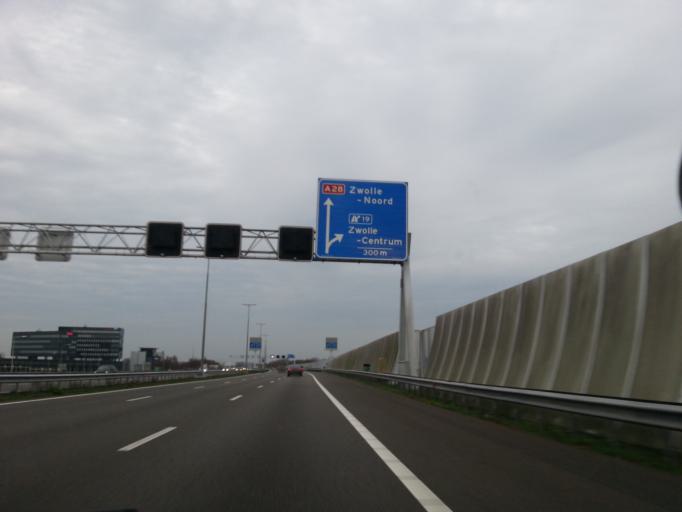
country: NL
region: Gelderland
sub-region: Gemeente Hattem
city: Hattem
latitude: 52.5046
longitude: 6.0638
